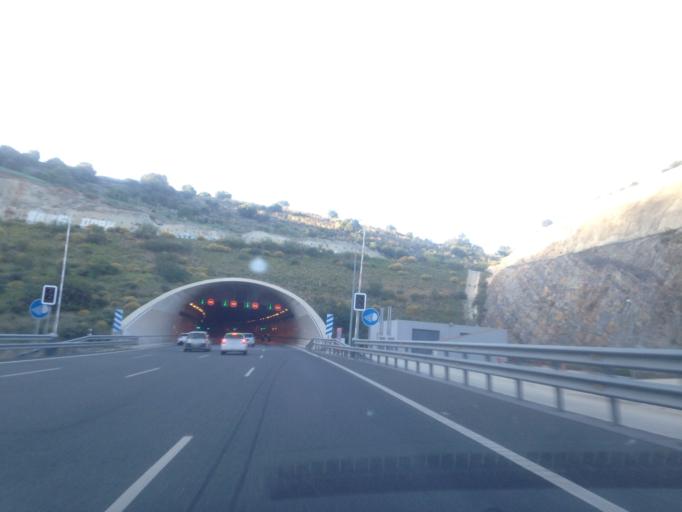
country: ES
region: Andalusia
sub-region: Provincia de Malaga
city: Torremolinos
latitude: 36.6483
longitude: -4.5125
